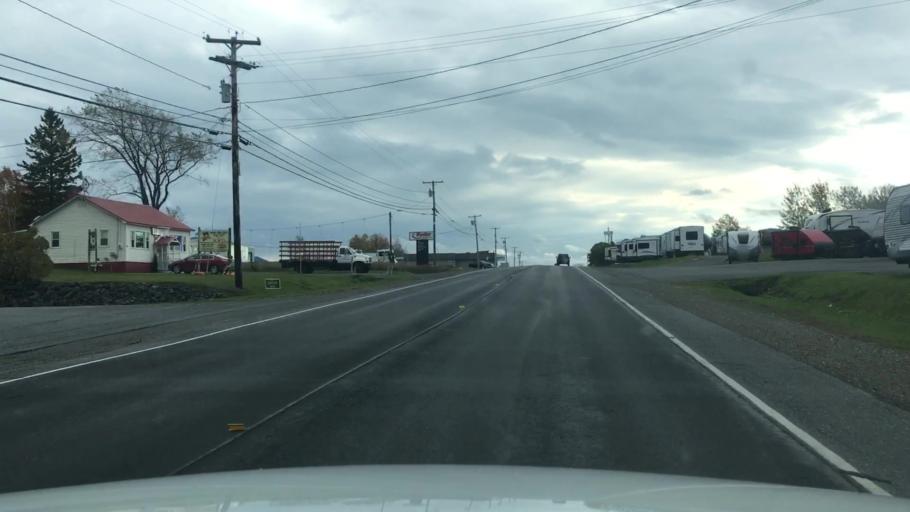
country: US
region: Maine
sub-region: Aroostook County
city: Presque Isle
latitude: 46.6606
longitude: -68.0081
